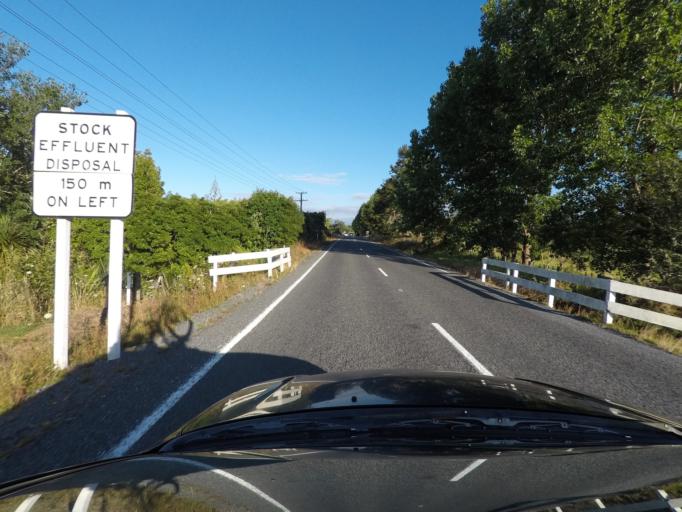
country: NZ
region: Northland
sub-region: Whangarei
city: Whangarei
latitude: -35.6453
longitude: 174.3024
